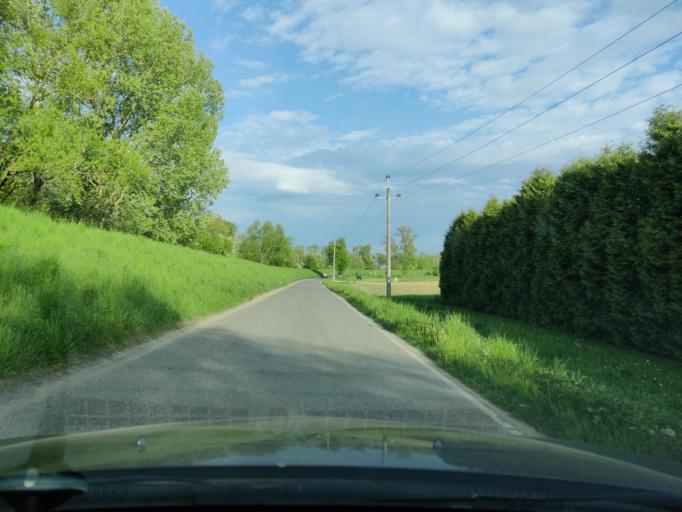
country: PL
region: Masovian Voivodeship
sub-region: Powiat otwocki
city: Jozefow
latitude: 52.1202
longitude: 21.1763
